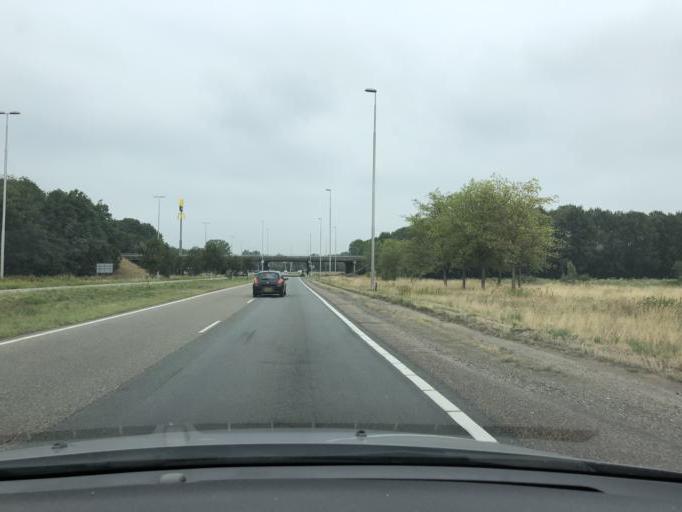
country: NL
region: Gelderland
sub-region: Gemeente Barneveld
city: Barneveld
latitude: 52.1658
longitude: 5.5663
